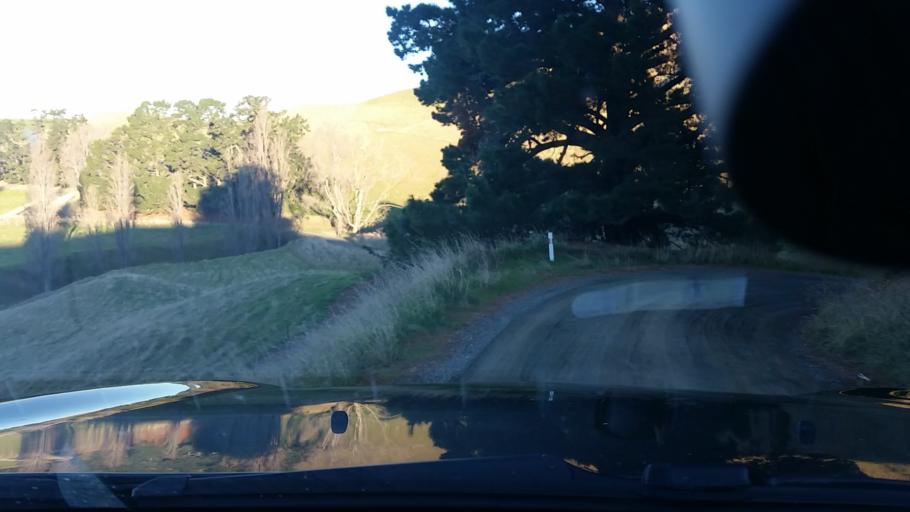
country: NZ
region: Marlborough
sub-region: Marlborough District
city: Blenheim
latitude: -41.7413
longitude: 174.0492
